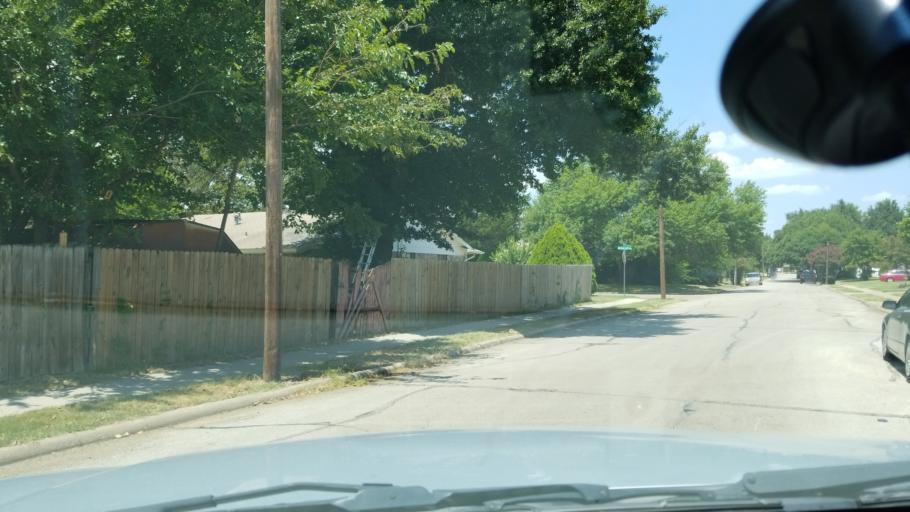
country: US
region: Texas
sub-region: Dallas County
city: Irving
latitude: 32.8242
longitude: -96.9879
